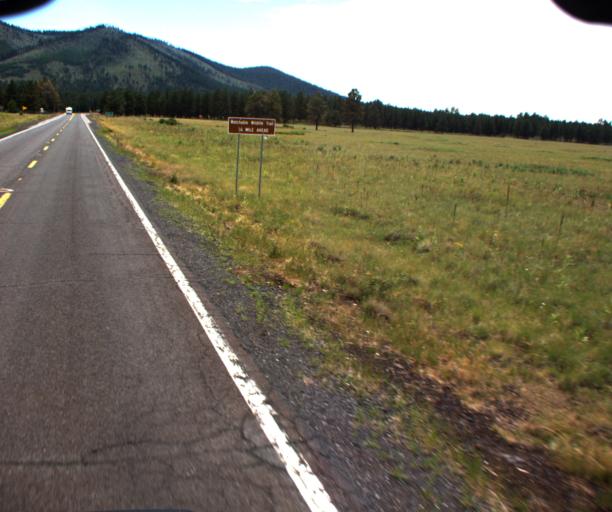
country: US
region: Arizona
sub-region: Coconino County
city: Flagstaff
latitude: 35.4061
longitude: -111.7556
